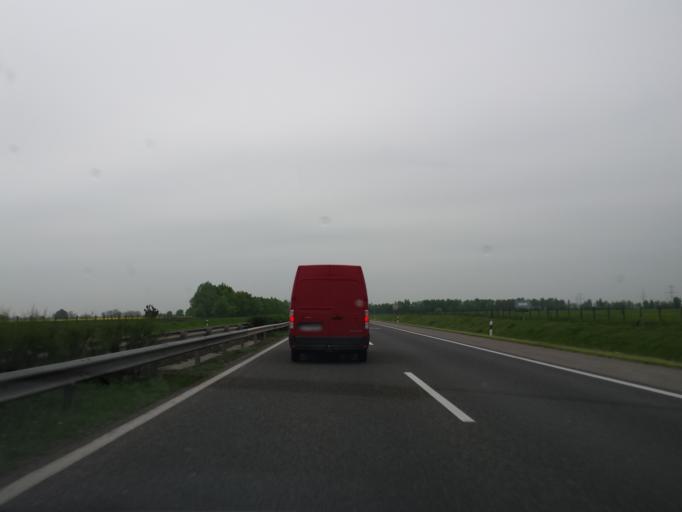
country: HU
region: Gyor-Moson-Sopron
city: Otteveny
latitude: 47.7222
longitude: 17.4614
